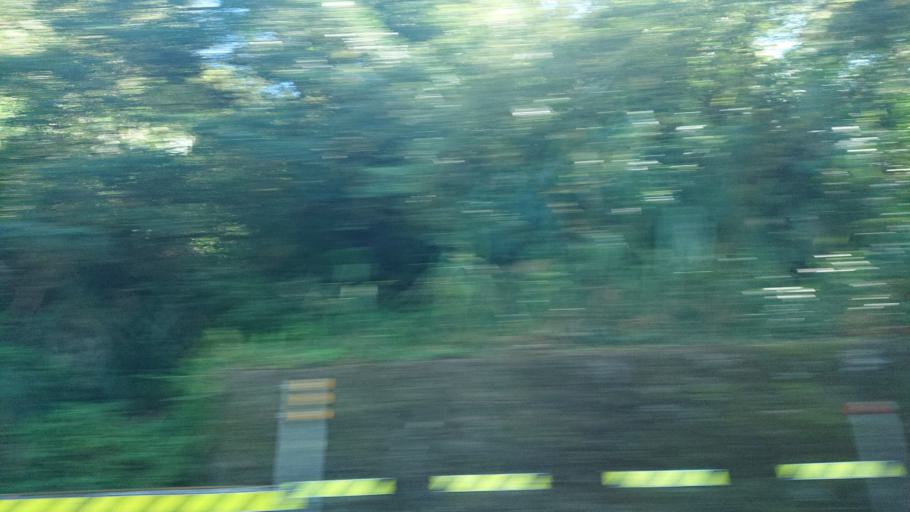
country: TW
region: Taiwan
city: Lugu
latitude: 23.4961
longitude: 120.7975
